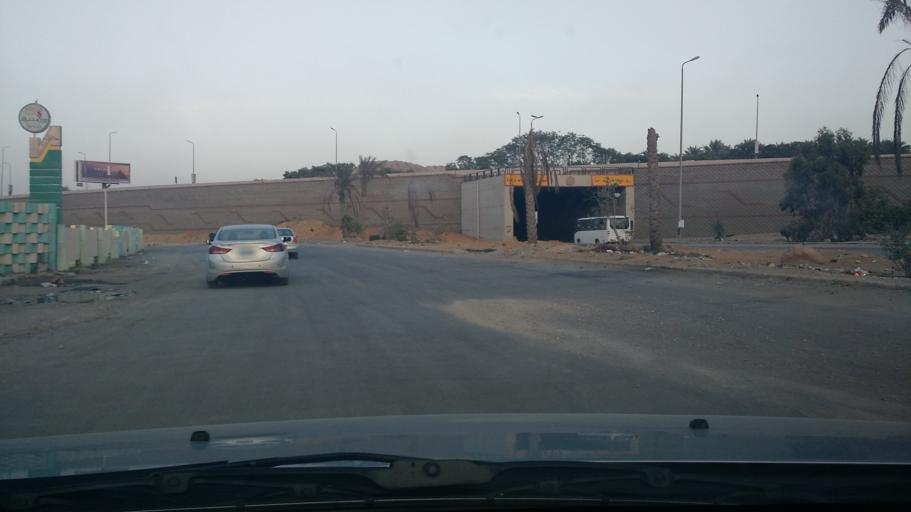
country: EG
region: Muhafazat al Qahirah
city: Cairo
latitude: 30.0243
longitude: 31.3542
